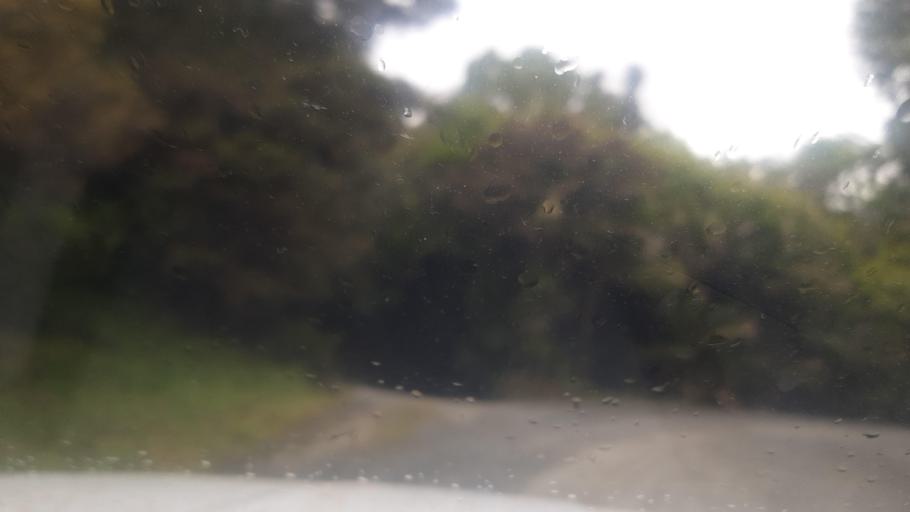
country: NZ
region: Northland
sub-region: Far North District
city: Taipa
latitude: -35.0927
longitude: 173.3951
